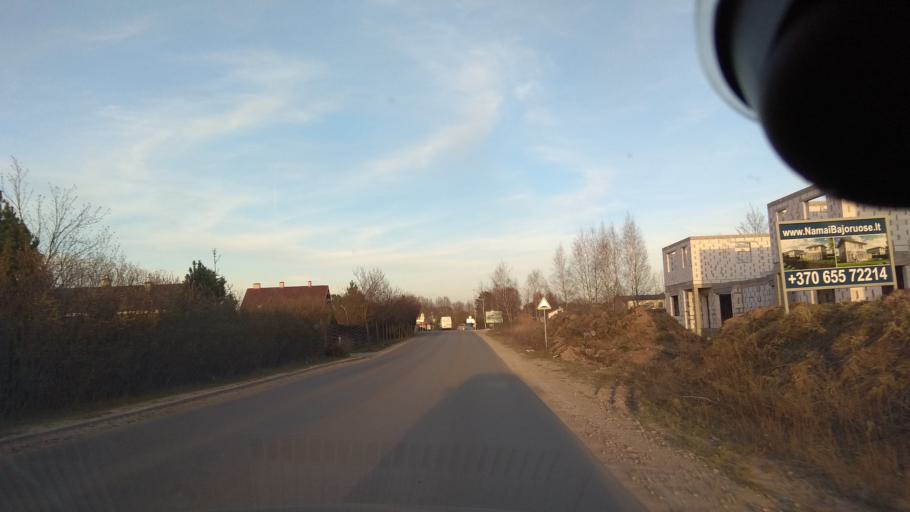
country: LT
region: Vilnius County
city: Pasilaiciai
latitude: 54.7577
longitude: 25.2276
